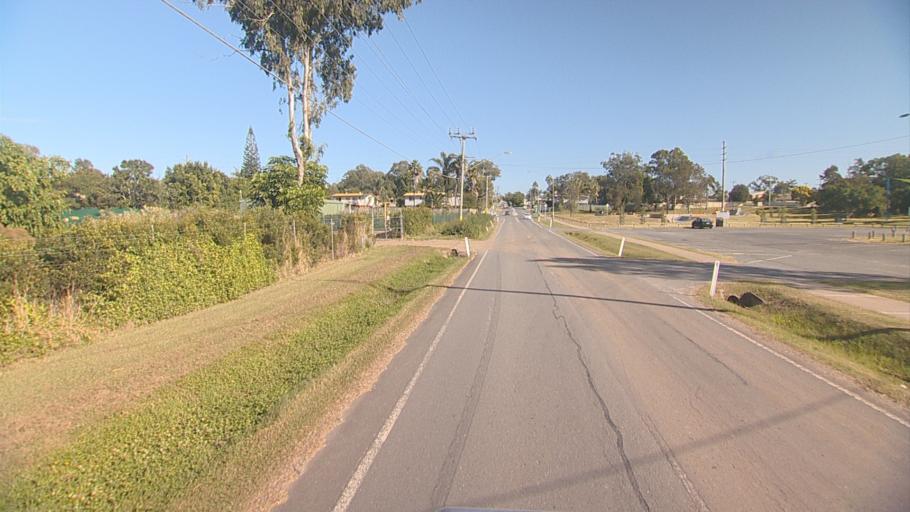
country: AU
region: Queensland
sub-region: Logan
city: Beenleigh
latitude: -27.6912
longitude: 153.1808
